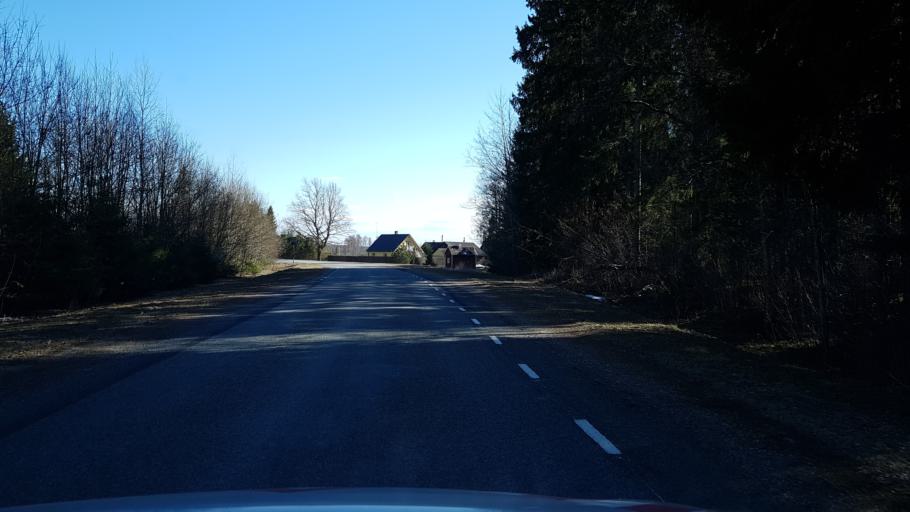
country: EE
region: Laeaene-Virumaa
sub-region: Kadrina vald
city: Kadrina
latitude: 59.3851
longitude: 26.0230
